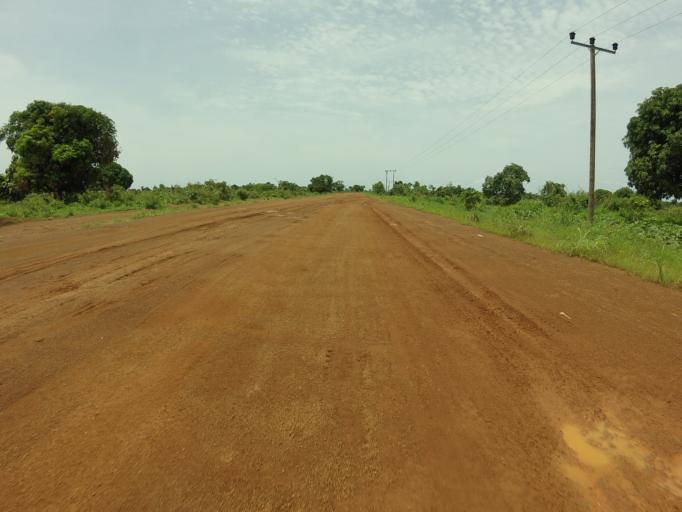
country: GH
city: Kpandae
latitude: 8.7531
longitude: 0.0703
